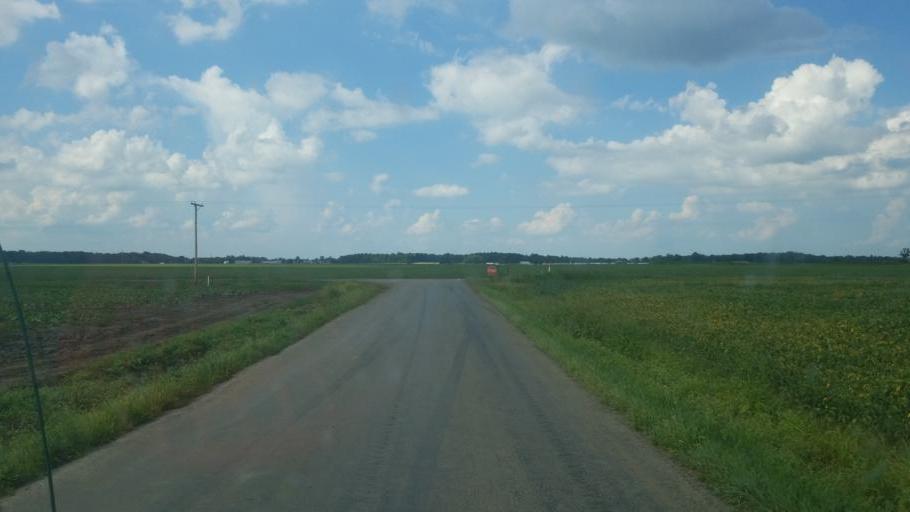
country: US
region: Ohio
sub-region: Huron County
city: Willard
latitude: 41.0181
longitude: -82.7092
